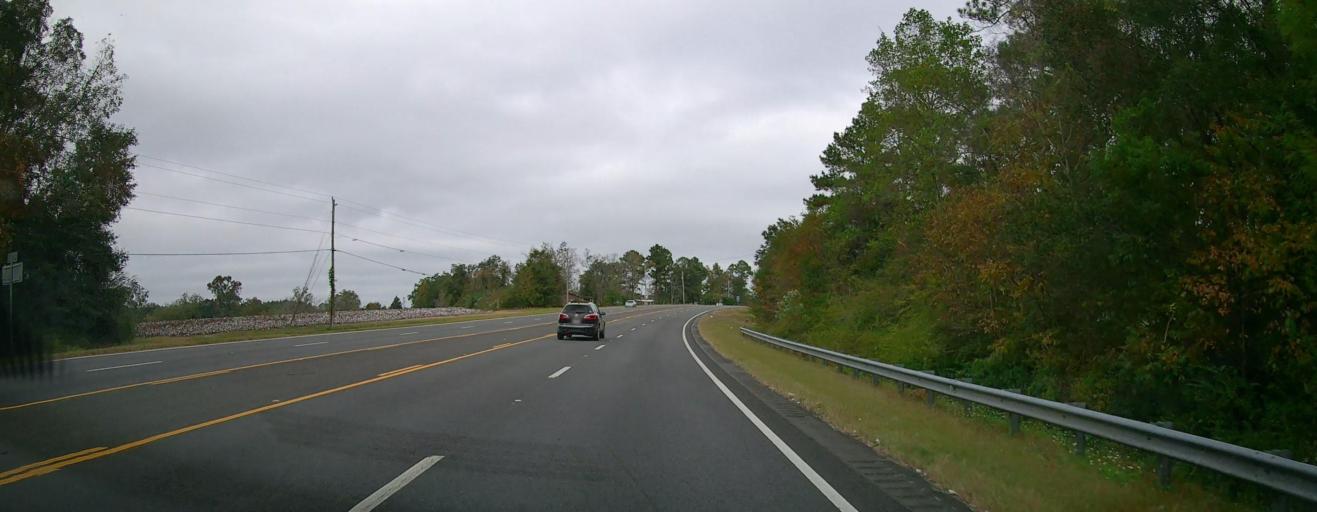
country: US
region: Georgia
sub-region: Thomas County
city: Thomasville
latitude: 30.9383
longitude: -83.9097
